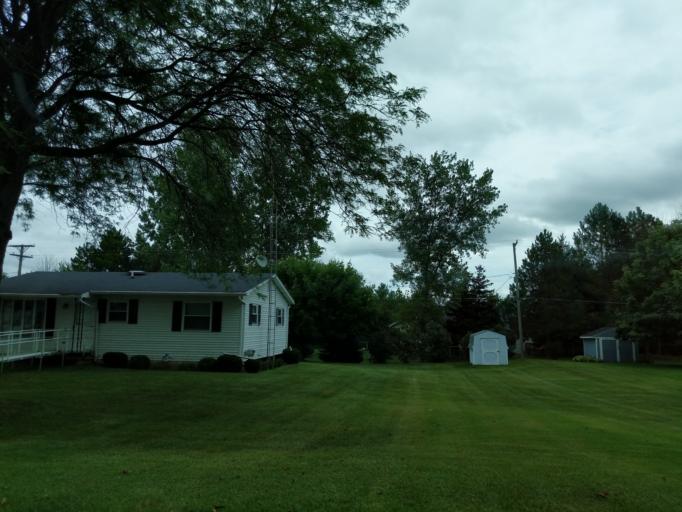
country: US
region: Michigan
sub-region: Lapeer County
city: Barnes Lake-Millers Lake
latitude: 43.3348
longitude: -83.3441
